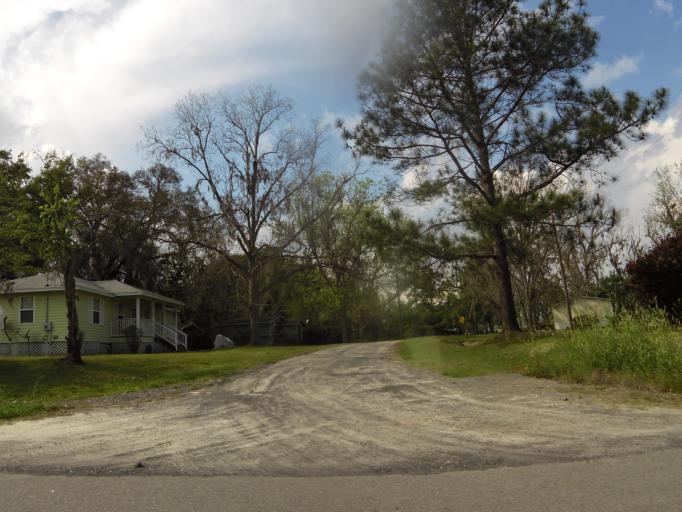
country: US
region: Georgia
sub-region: Charlton County
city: Folkston
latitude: 30.8259
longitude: -82.0387
